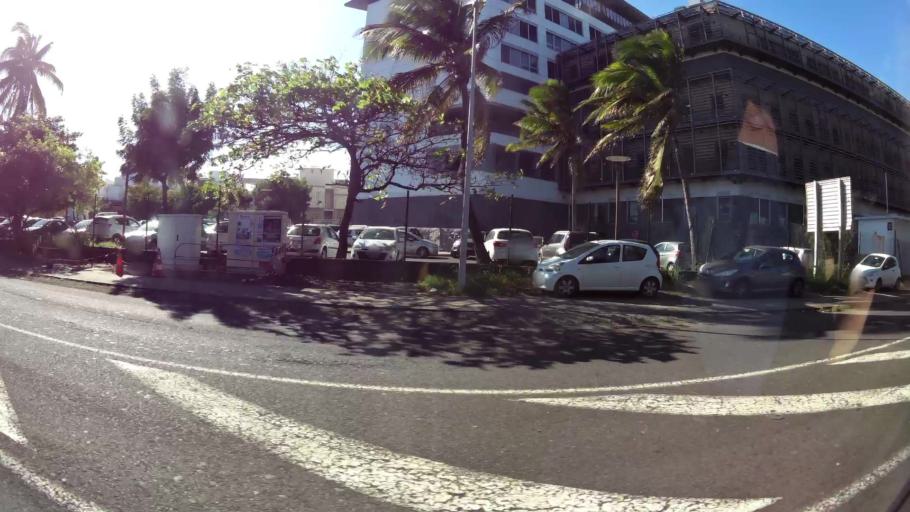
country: RE
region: Reunion
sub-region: Reunion
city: Saint-Pierre
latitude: -21.3471
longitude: 55.4915
